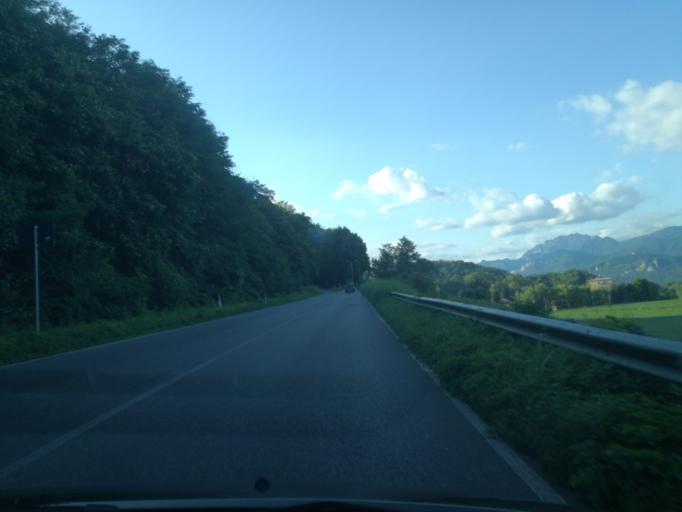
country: IT
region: Lombardy
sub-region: Provincia di Lecco
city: Imbersago
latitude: 45.6999
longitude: 9.4449
